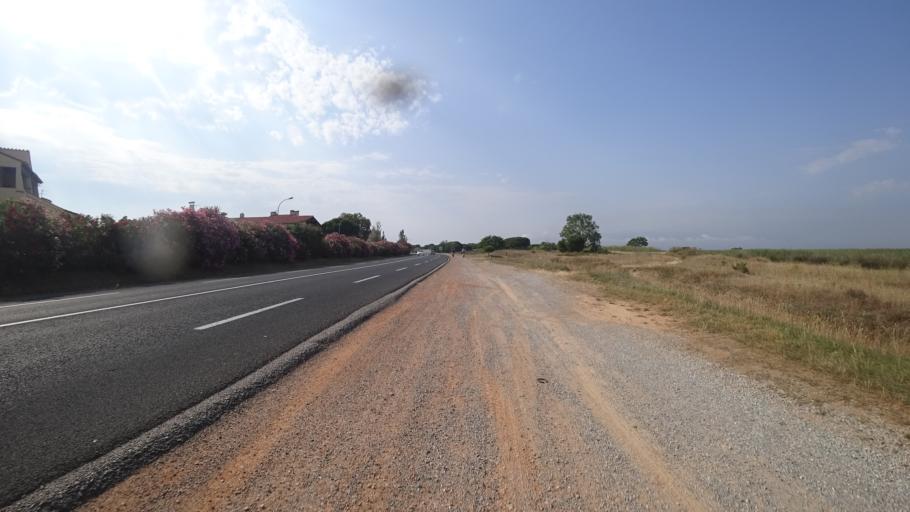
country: FR
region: Languedoc-Roussillon
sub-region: Departement des Pyrenees-Orientales
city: Canet-en-Roussillon
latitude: 42.6799
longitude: 3.0285
